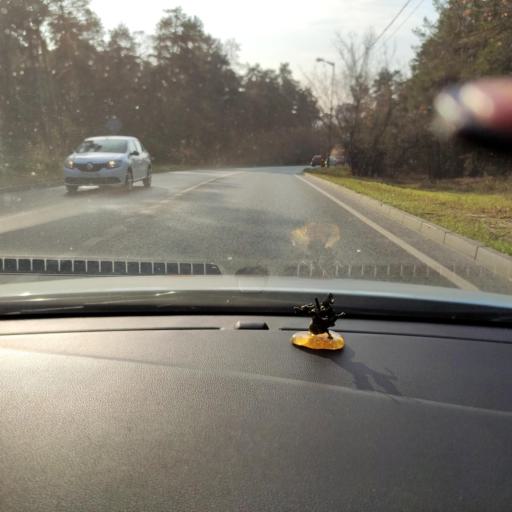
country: RU
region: Tatarstan
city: Osinovo
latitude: 55.8252
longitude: 48.8972
